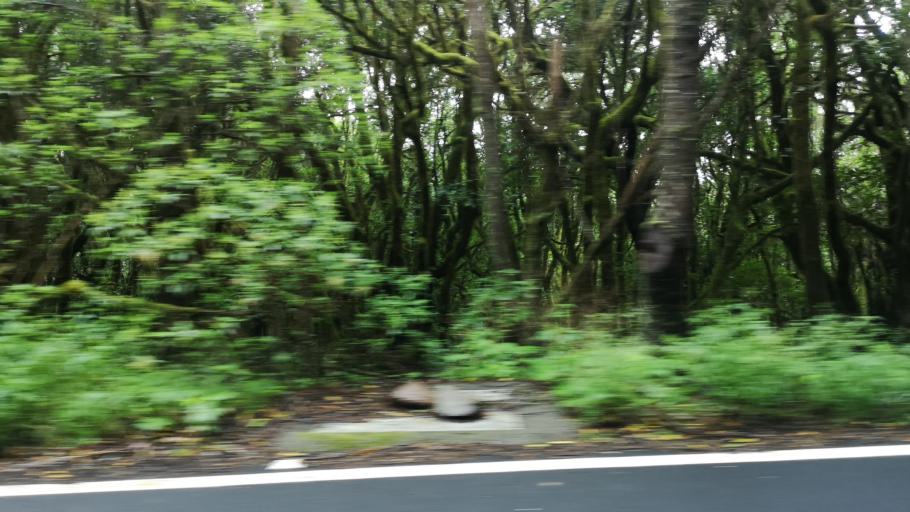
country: ES
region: Canary Islands
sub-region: Provincia de Santa Cruz de Tenerife
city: Vallehermosa
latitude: 28.1478
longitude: -17.2911
